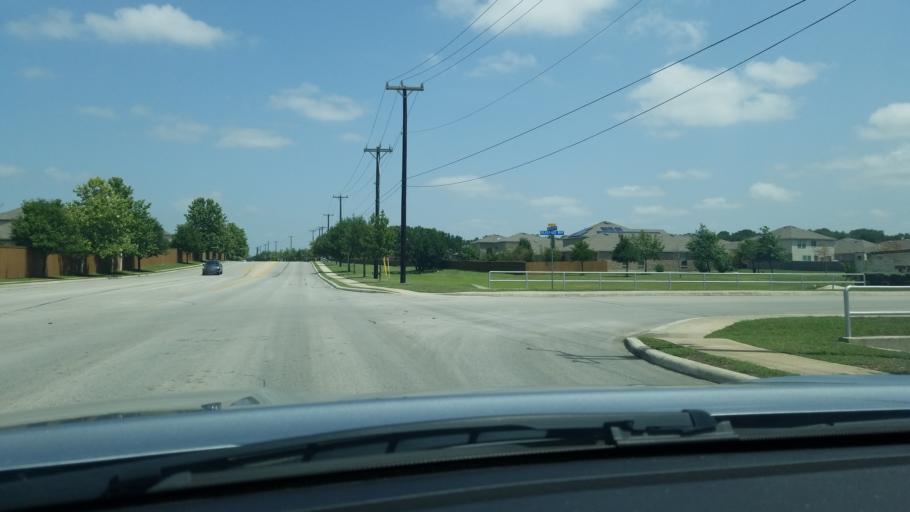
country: US
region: Texas
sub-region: Bexar County
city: Timberwood Park
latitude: 29.7021
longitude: -98.4817
